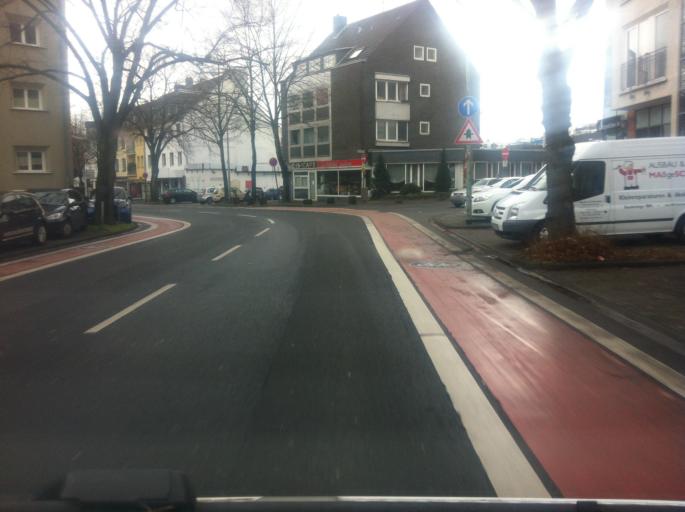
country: DE
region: North Rhine-Westphalia
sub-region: Regierungsbezirk Koln
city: Nippes
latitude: 50.9753
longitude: 6.9483
